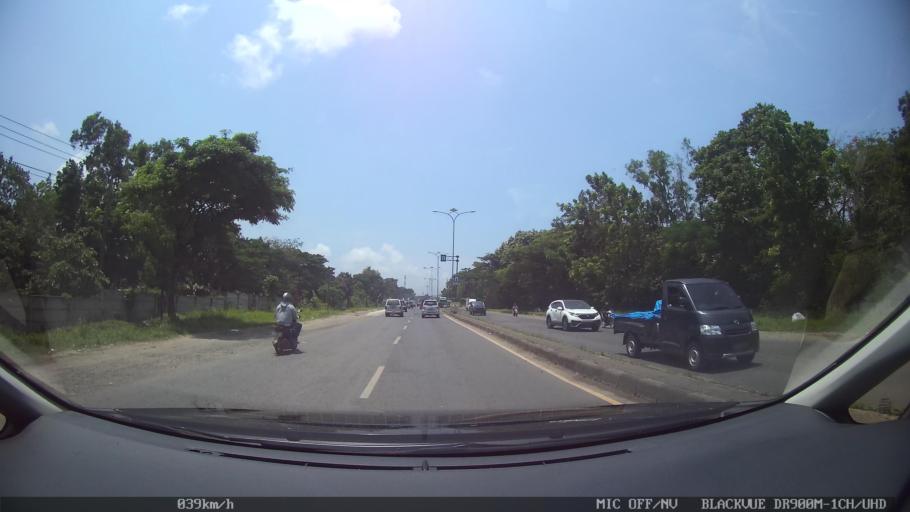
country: ID
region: Lampung
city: Kedaton
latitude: -5.3785
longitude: 105.2823
